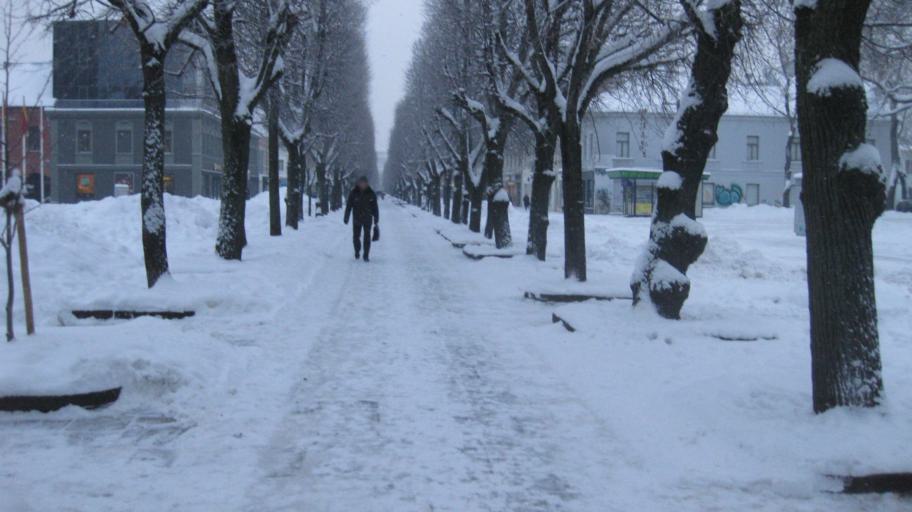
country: LT
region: Kauno apskritis
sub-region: Kaunas
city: Kaunas
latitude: 54.8977
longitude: 23.9054
